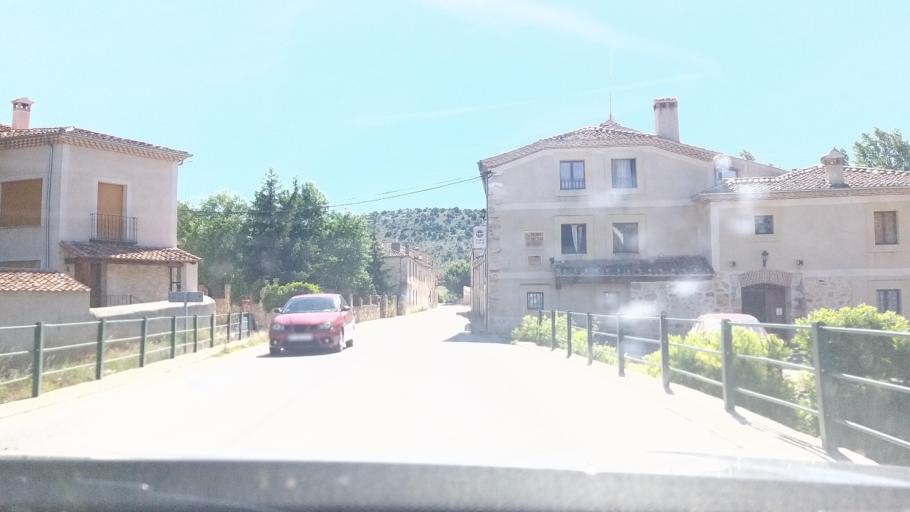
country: ES
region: Castille and Leon
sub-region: Provincia de Segovia
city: Pedraza
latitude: 41.1422
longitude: -3.8278
